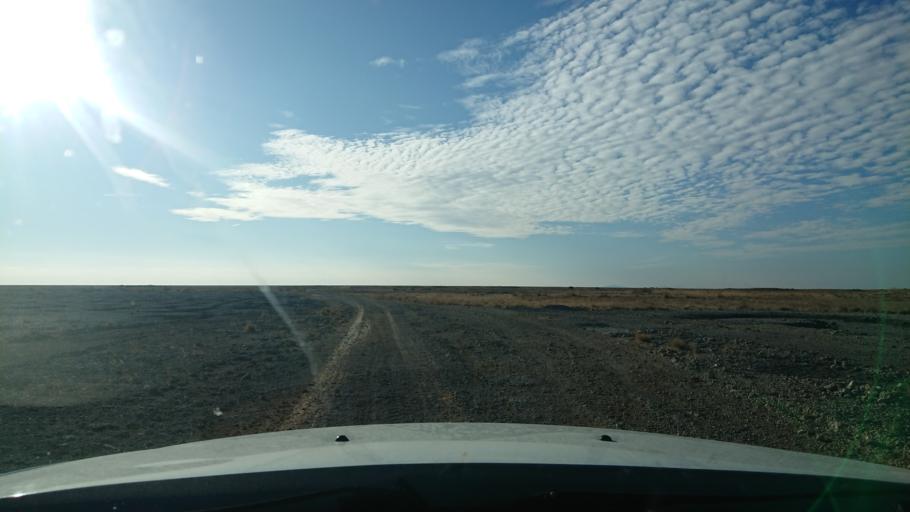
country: TR
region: Aksaray
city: Eskil
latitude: 38.5421
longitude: 33.3498
